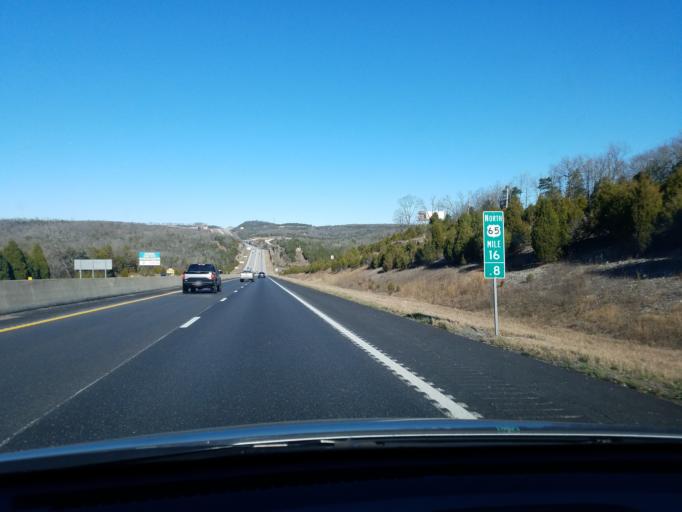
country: US
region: Missouri
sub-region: Taney County
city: Merriam Woods
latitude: 36.7210
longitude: -93.2207
